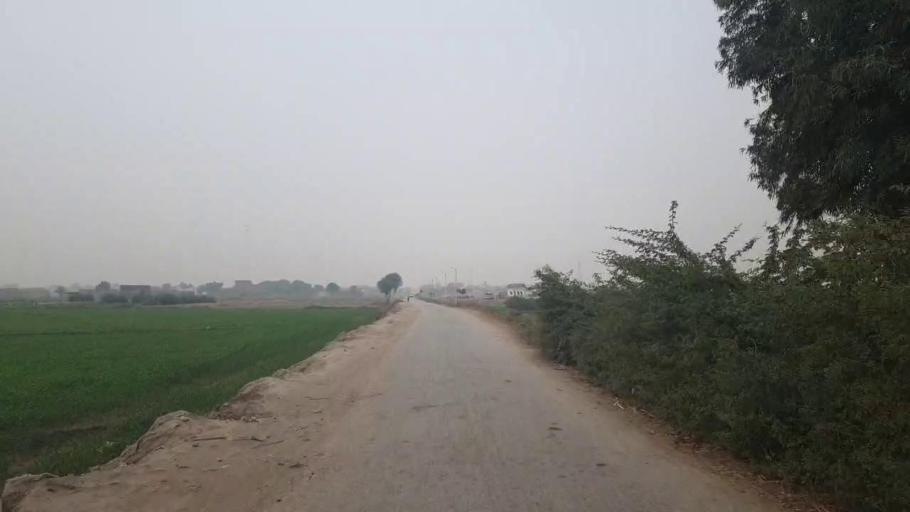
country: PK
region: Sindh
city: Tando Adam
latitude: 25.7499
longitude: 68.6709
